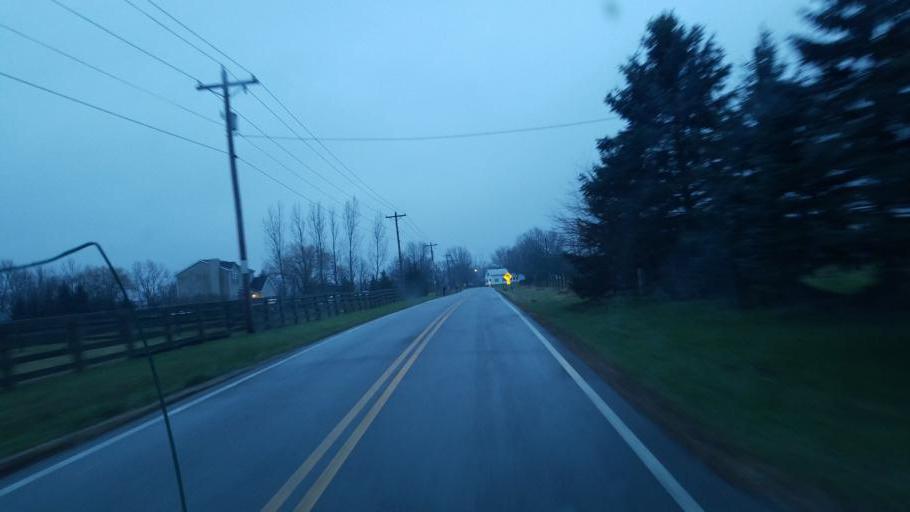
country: US
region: Ohio
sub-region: Delaware County
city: Ashley
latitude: 40.3918
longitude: -82.9482
